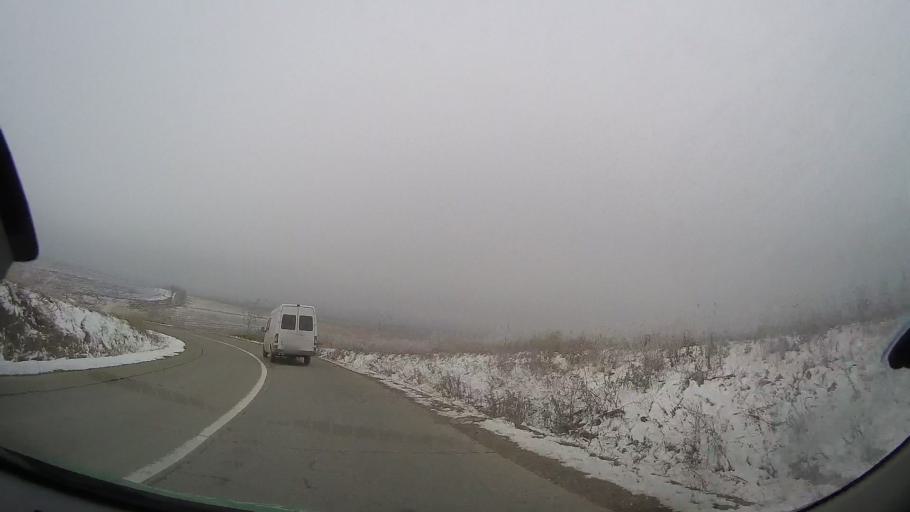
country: RO
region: Vaslui
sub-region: Comuna Grivita
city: Grivita
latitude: 46.1940
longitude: 27.6038
